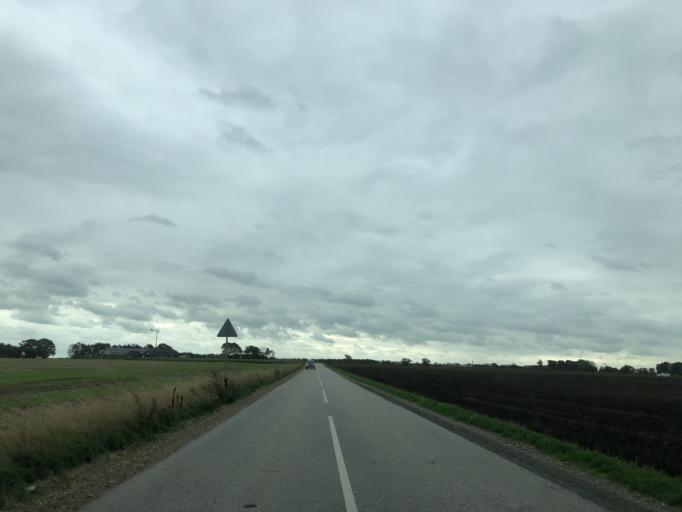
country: DK
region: Central Jutland
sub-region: Herning Kommune
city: Snejbjerg
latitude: 56.1504
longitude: 8.8940
